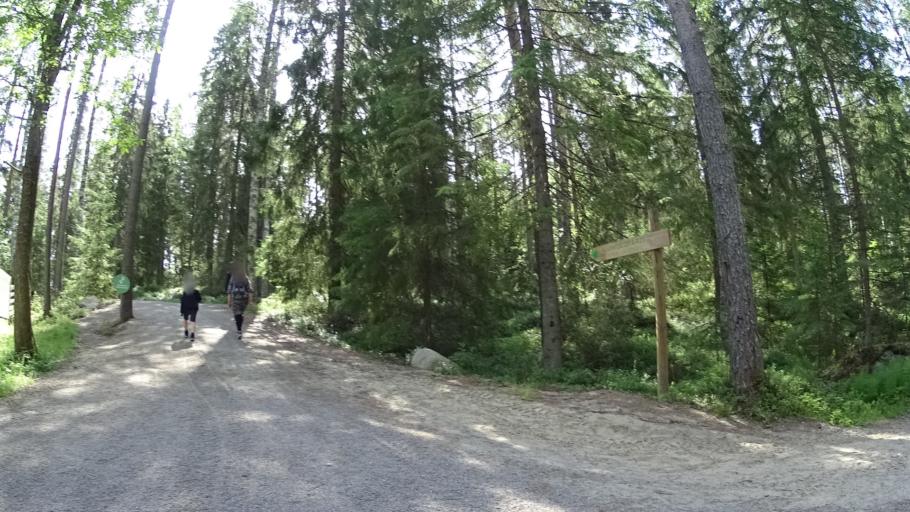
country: FI
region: Southern Ostrobothnia
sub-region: Kuusiokunnat
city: AEhtaeri
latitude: 62.5389
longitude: 24.1843
